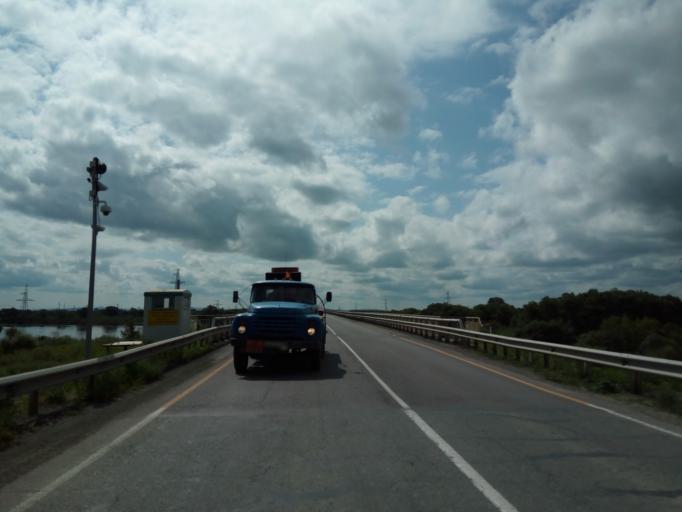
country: RU
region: Primorskiy
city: Dal'nerechensk
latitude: 45.9648
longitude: 133.7830
